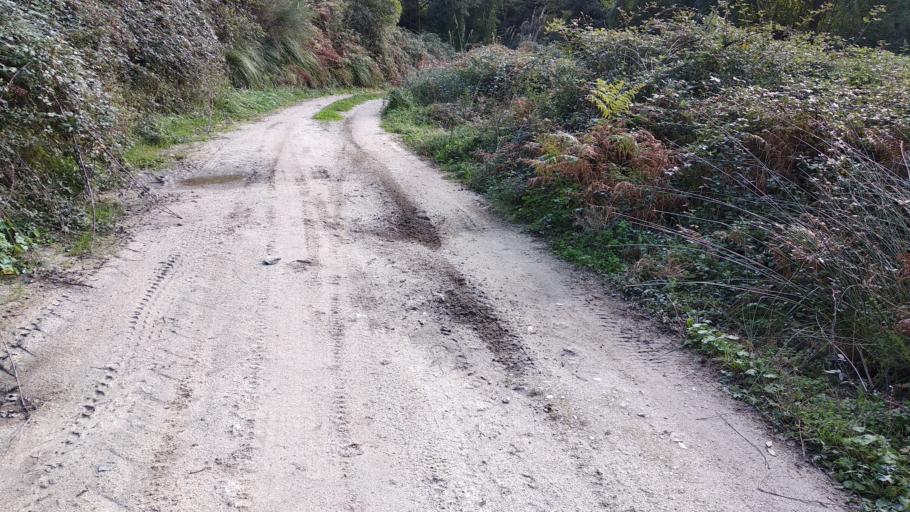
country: IT
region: Calabria
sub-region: Provincia di Reggio Calabria
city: San Roberto
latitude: 38.2406
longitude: 15.7770
